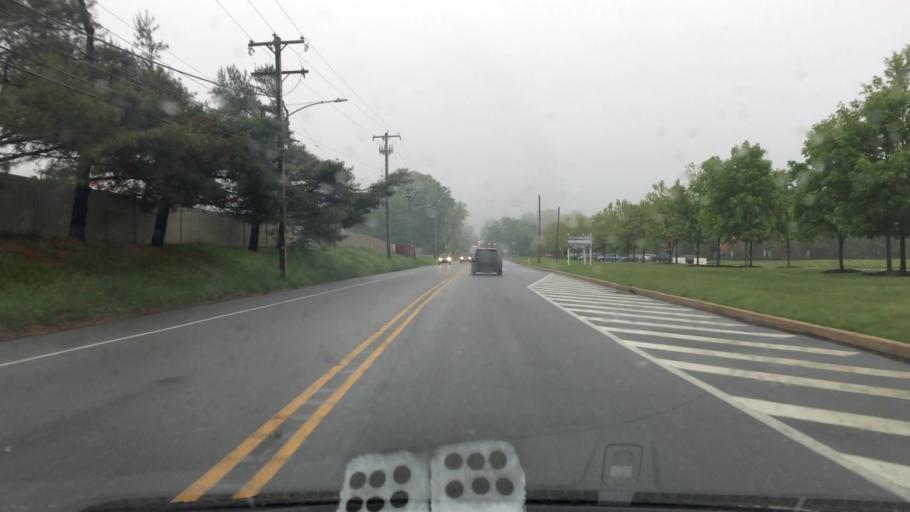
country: US
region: Pennsylvania
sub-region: Delaware County
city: Village Green-Green Ridge
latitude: 39.8561
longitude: -75.4269
